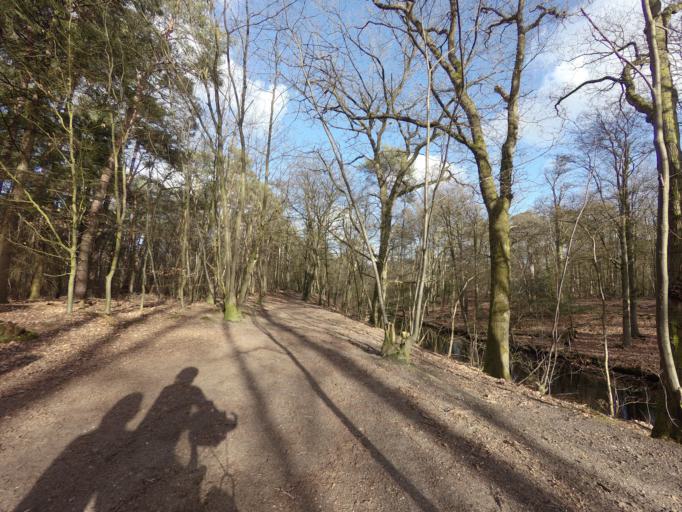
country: NL
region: North Holland
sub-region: Gemeente Bussum
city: Bussum
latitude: 52.2434
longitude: 5.1478
